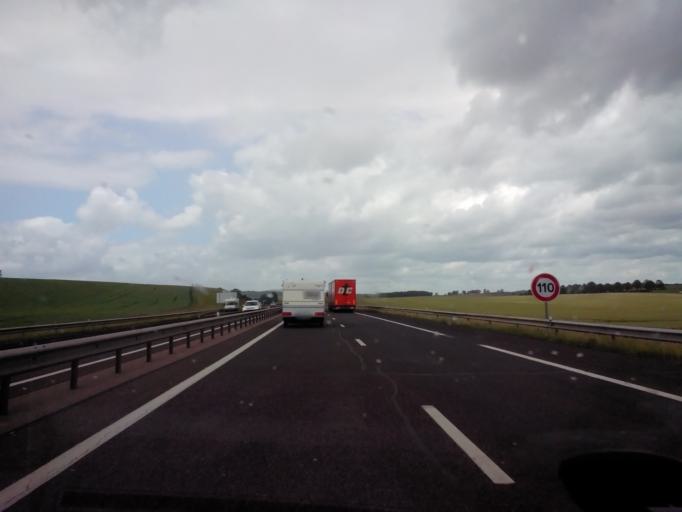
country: FR
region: Lorraine
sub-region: Departement de Meurthe-et-Moselle
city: Blenod-les-Toul
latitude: 48.6149
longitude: 5.8868
